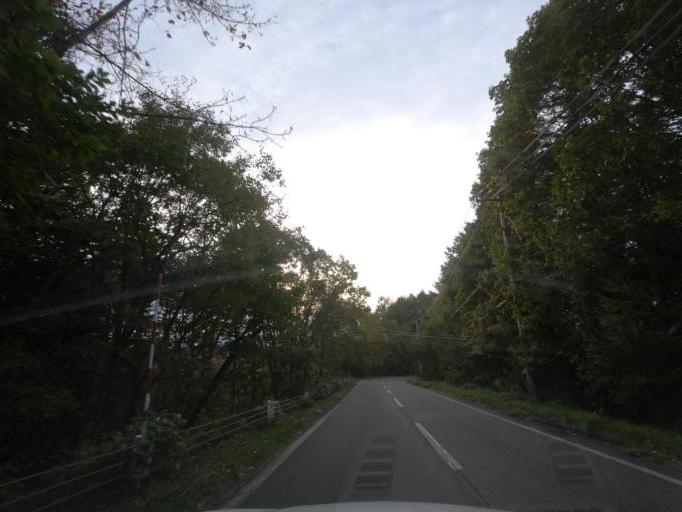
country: JP
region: Hokkaido
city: Obihiro
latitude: 42.5444
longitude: 143.4080
